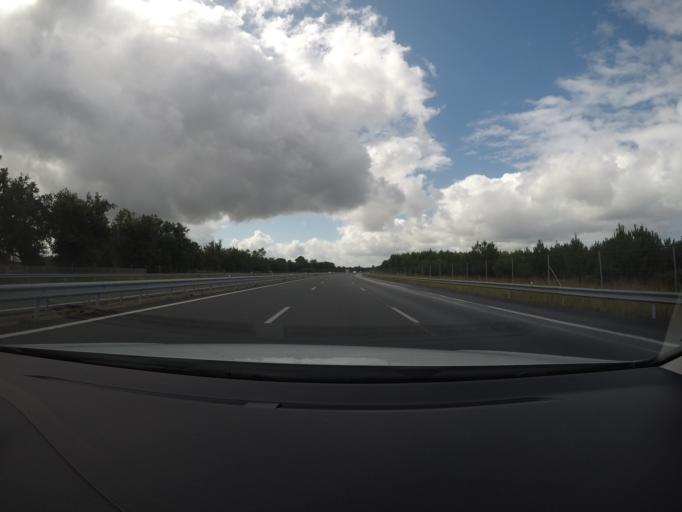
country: FR
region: Aquitaine
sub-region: Departement des Landes
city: Ychoux
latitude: 44.3281
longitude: -0.8729
